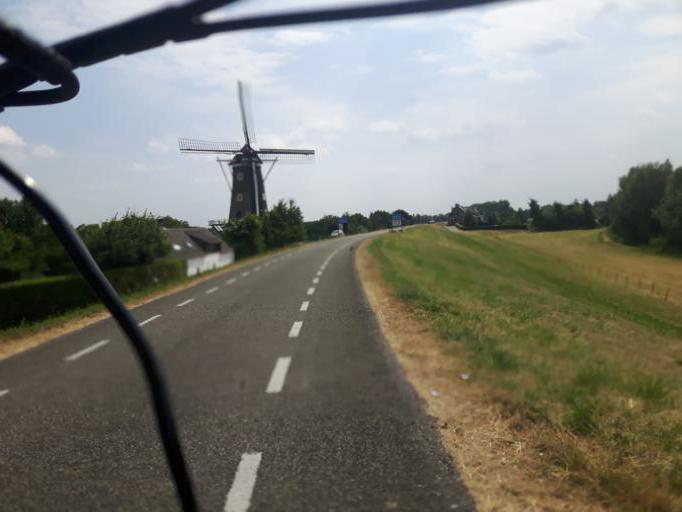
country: NL
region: Gelderland
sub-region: Gemeente Zaltbommel
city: Zaltbommel
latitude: 51.8147
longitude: 5.2093
